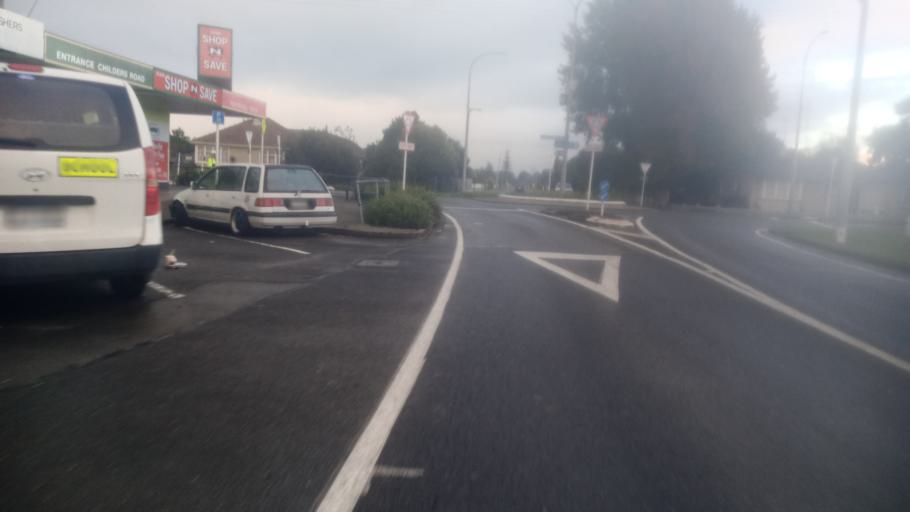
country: NZ
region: Gisborne
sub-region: Gisborne District
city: Gisborne
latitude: -38.6567
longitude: 177.9958
